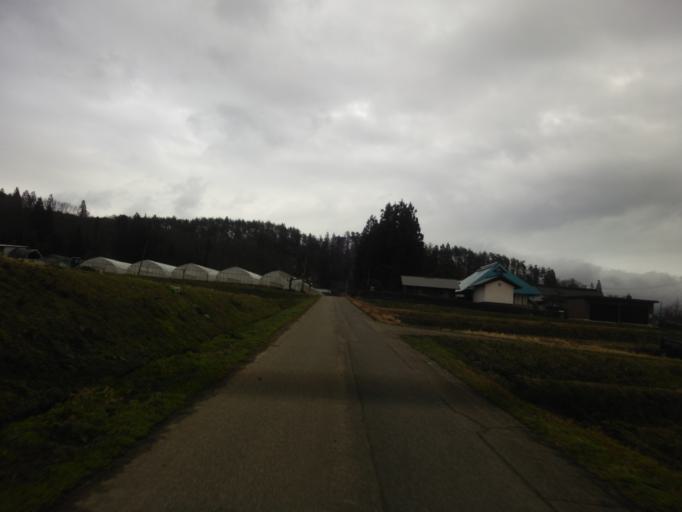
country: JP
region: Fukushima
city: Kitakata
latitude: 37.6690
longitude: 139.9163
